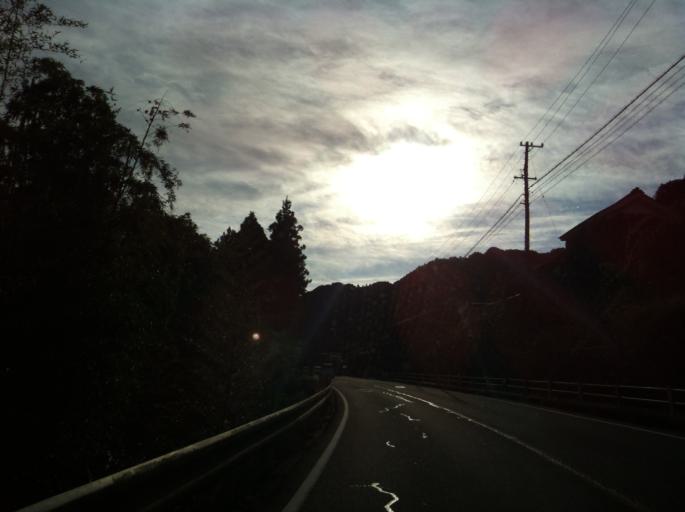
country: JP
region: Gifu
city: Mitake
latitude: 35.5454
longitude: 137.1572
